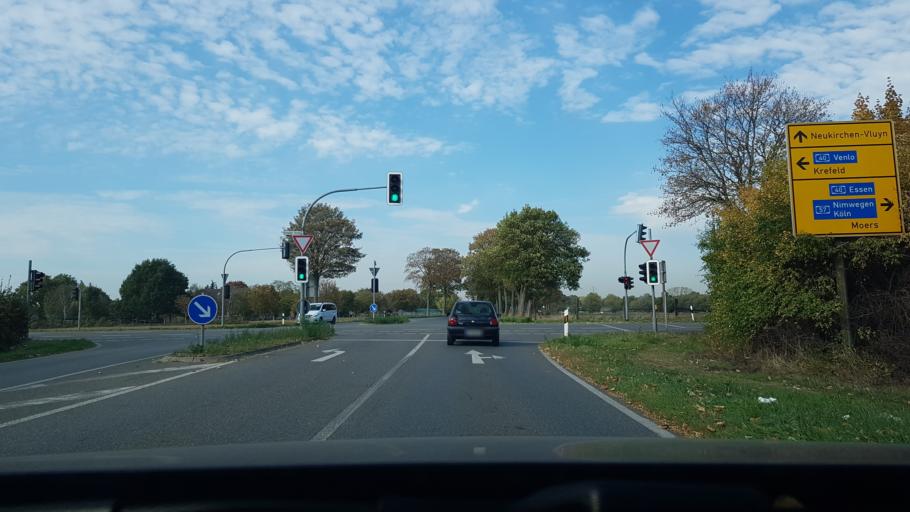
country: DE
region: North Rhine-Westphalia
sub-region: Regierungsbezirk Dusseldorf
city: Moers
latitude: 51.4211
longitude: 6.5829
